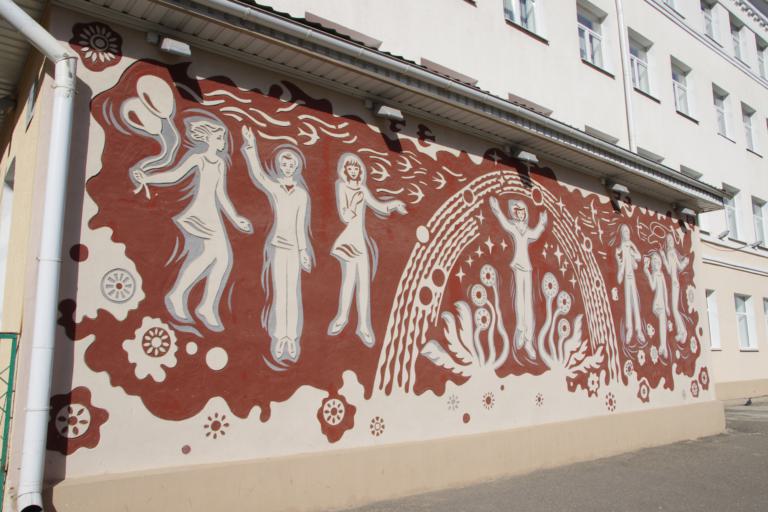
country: BY
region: Vitebsk
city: Vitebsk
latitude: 55.2040
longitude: 30.2156
